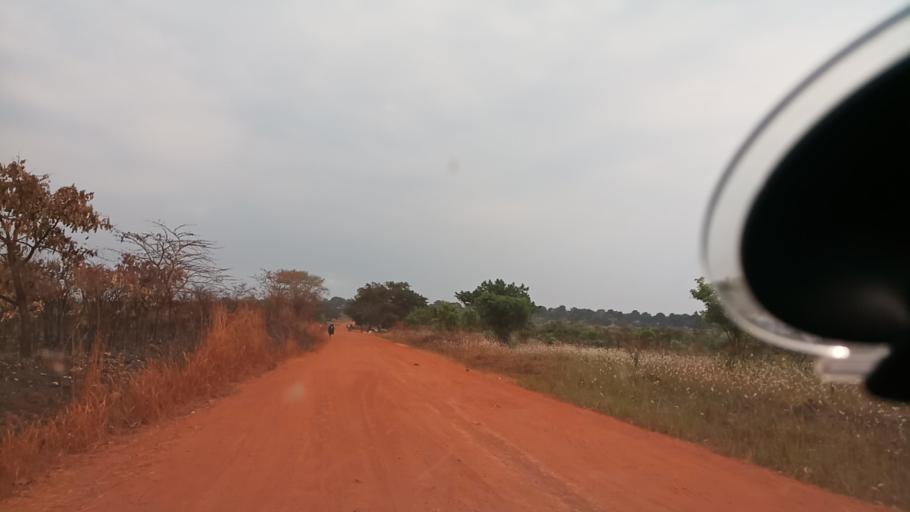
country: ZM
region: Luapula
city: Nchelenge
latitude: -9.1084
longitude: 28.3025
